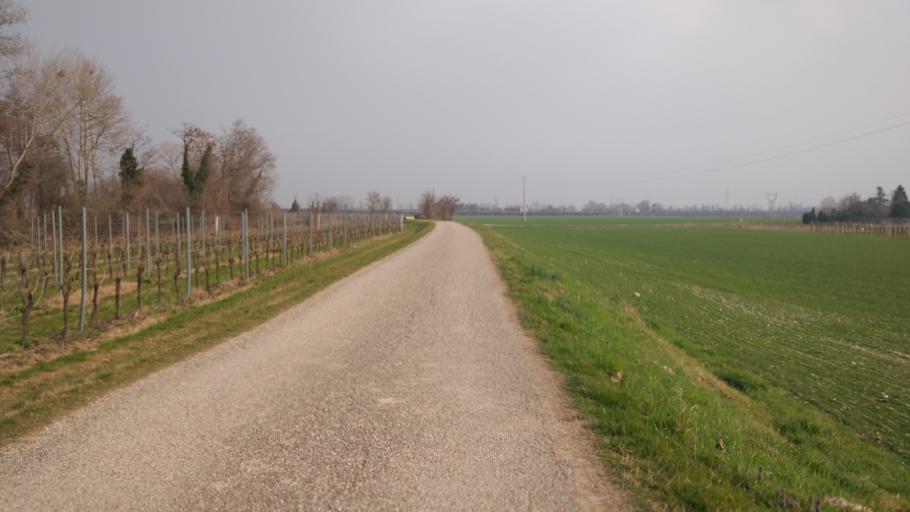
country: IT
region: Veneto
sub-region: Provincia di Verona
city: Caldierino-Rota
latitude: 45.3954
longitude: 11.1432
